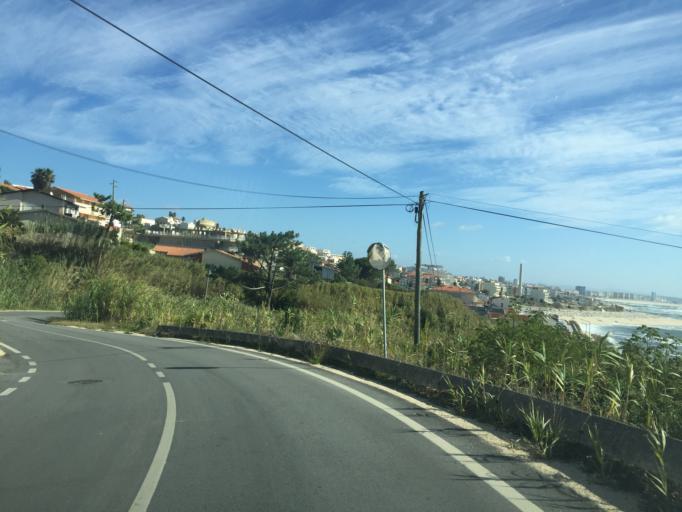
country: PT
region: Coimbra
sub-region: Figueira da Foz
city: Buarcos
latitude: 40.1783
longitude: -8.9012
